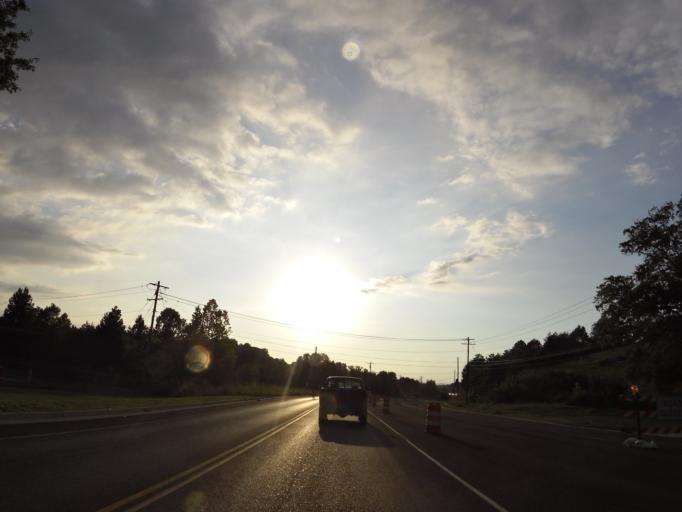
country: US
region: Tennessee
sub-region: Cocke County
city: Newport
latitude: 35.9705
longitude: -83.2703
